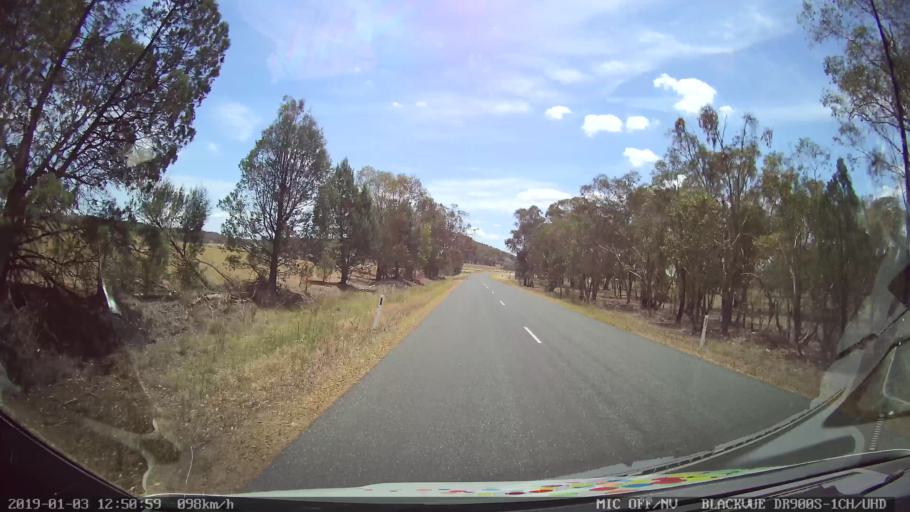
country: AU
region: New South Wales
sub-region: Weddin
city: Grenfell
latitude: -33.6849
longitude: 148.2755
